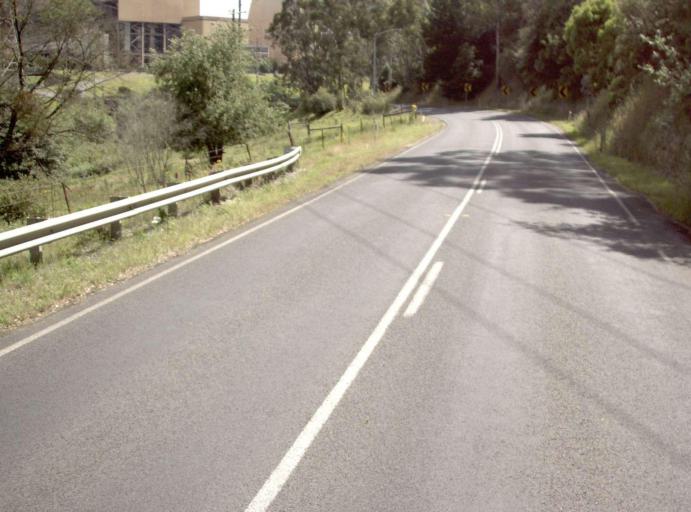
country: AU
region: Victoria
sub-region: Latrobe
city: Morwell
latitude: -38.1722
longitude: 146.3473
